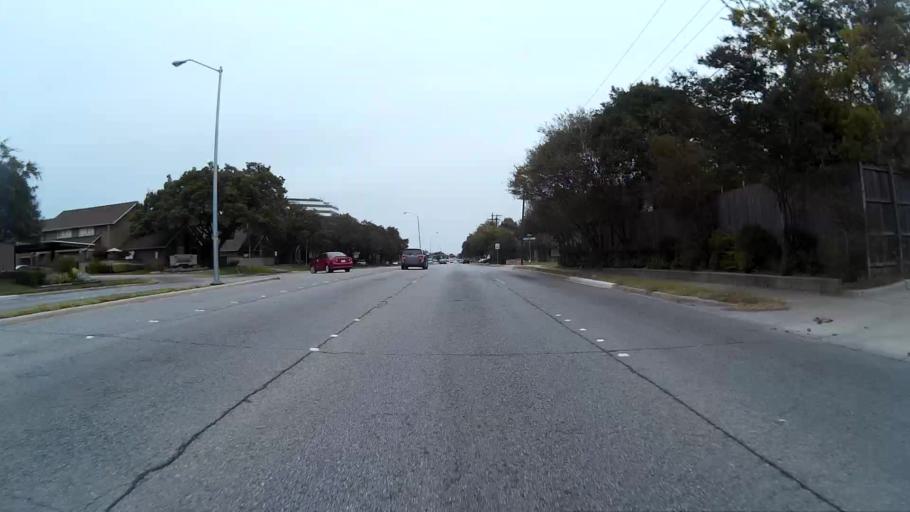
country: US
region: Texas
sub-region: Dallas County
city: Richardson
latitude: 32.9470
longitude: -96.7688
